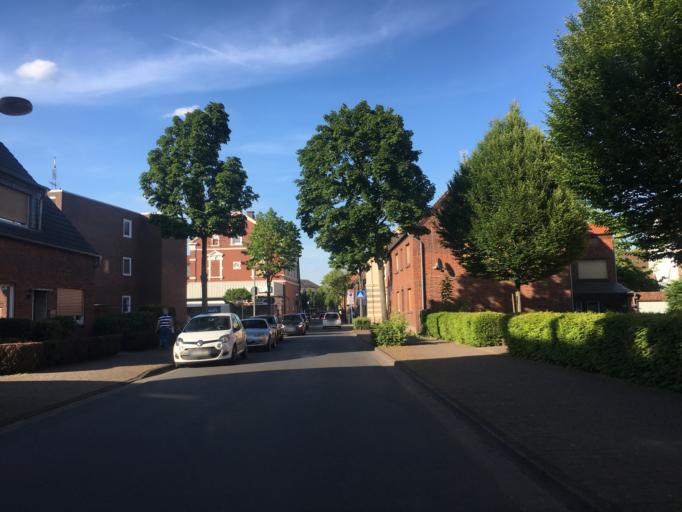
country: DE
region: North Rhine-Westphalia
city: Olfen
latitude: 51.7059
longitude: 7.3772
